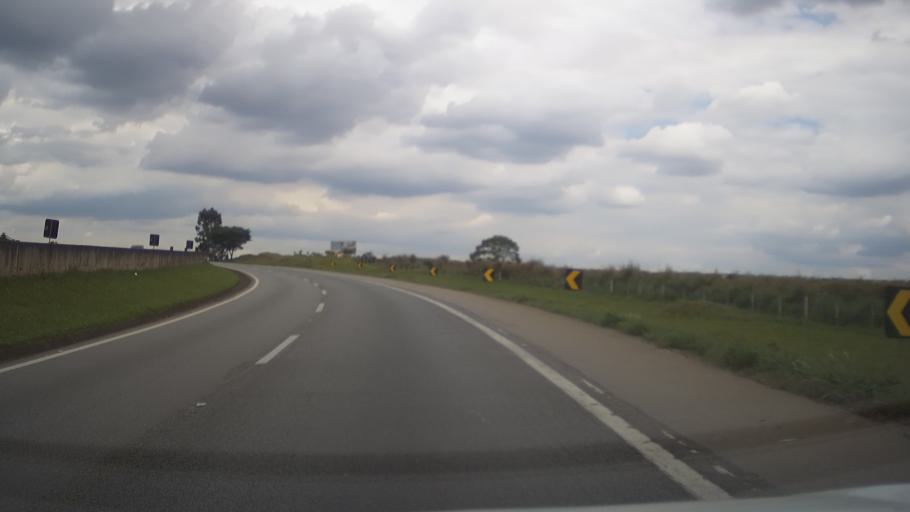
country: BR
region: Minas Gerais
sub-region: Tres Coracoes
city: Tres Coracoes
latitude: -21.4892
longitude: -45.2074
